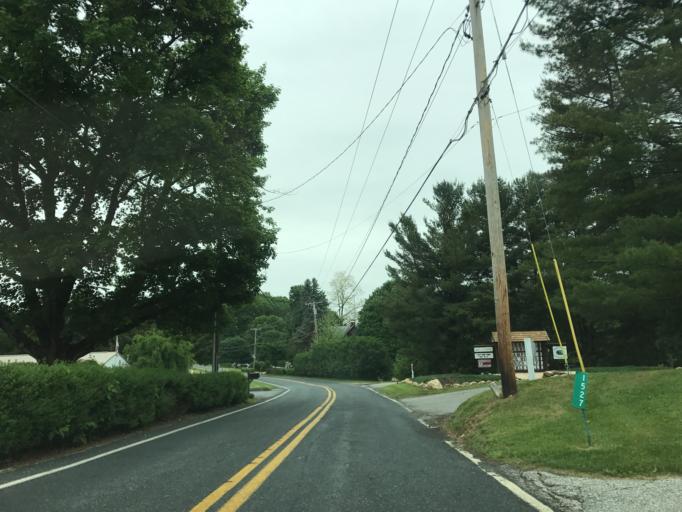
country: US
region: Pennsylvania
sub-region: York County
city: New Freedom
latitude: 39.6951
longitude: -76.6988
